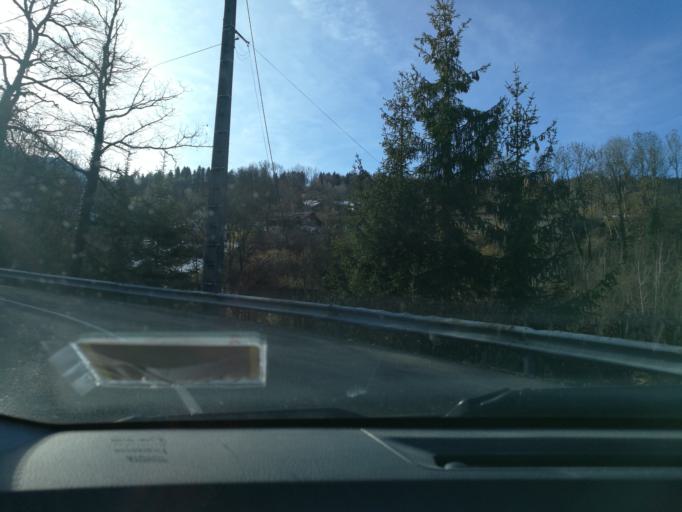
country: FR
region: Rhone-Alpes
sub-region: Departement de la Haute-Savoie
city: Saint-Gervais-les-Bains
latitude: 45.9025
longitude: 6.6992
